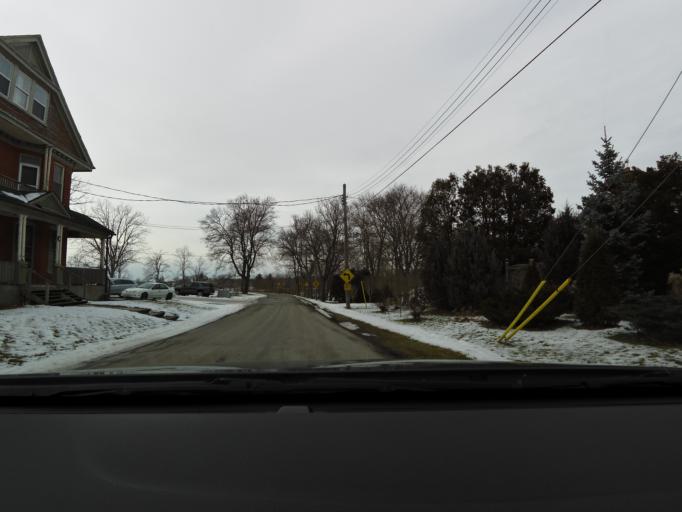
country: CA
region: Ontario
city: Ancaster
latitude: 42.9516
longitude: -79.8583
